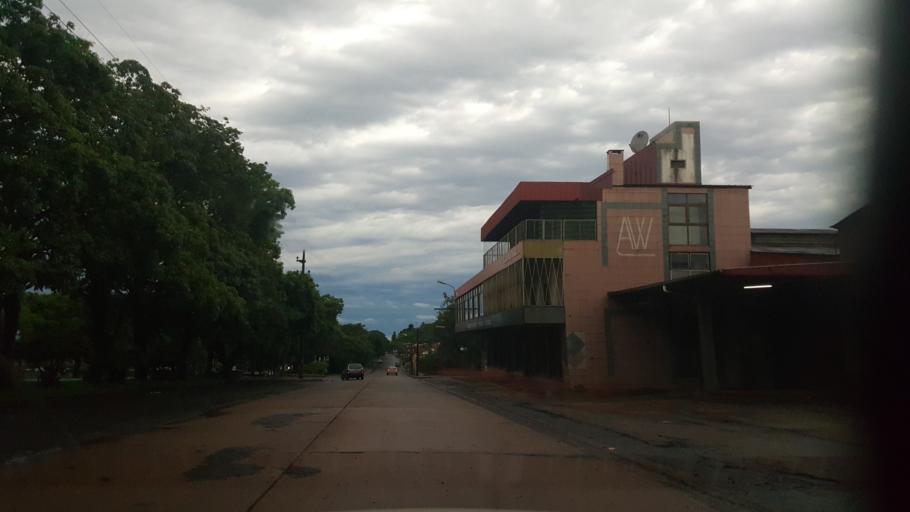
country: AR
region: Misiones
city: Jardin America
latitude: -27.0459
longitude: -55.2396
